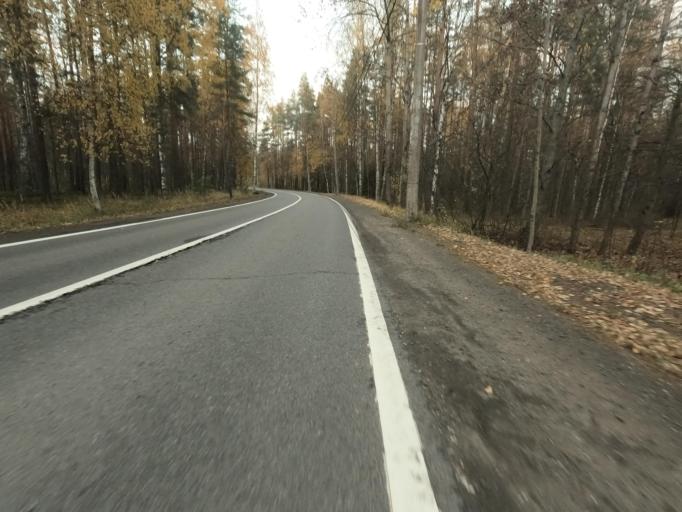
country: RU
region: St.-Petersburg
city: Repino
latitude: 60.1865
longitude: 29.8636
